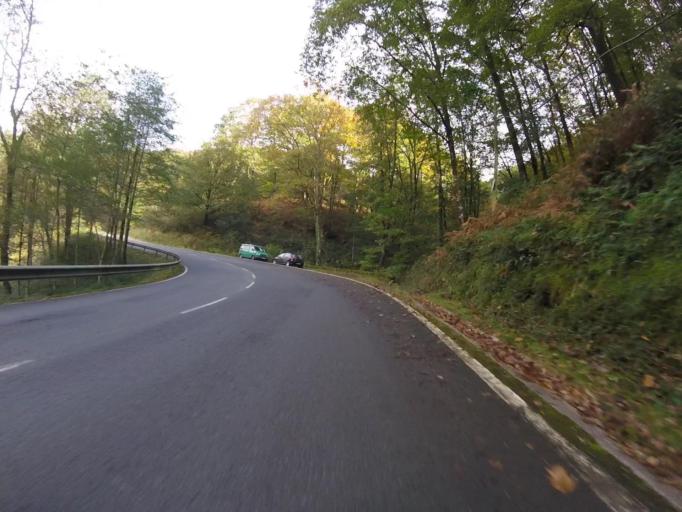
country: ES
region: Navarre
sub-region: Provincia de Navarra
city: Goizueta
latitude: 43.2004
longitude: -1.8571
